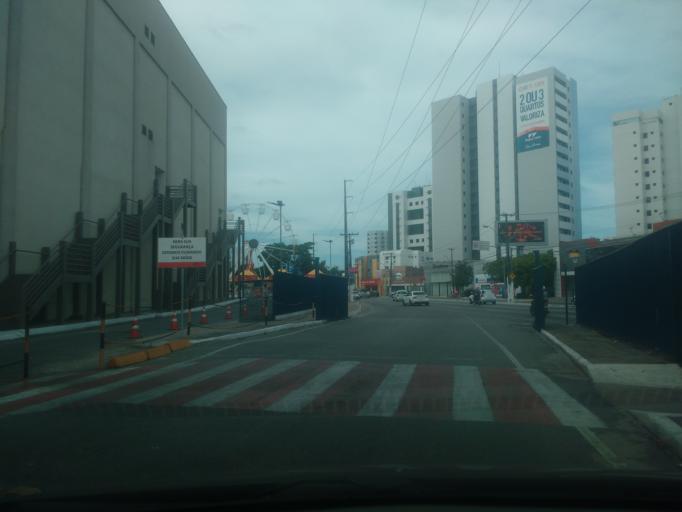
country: BR
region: Alagoas
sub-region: Maceio
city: Maceio
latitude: -9.6483
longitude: -35.7137
